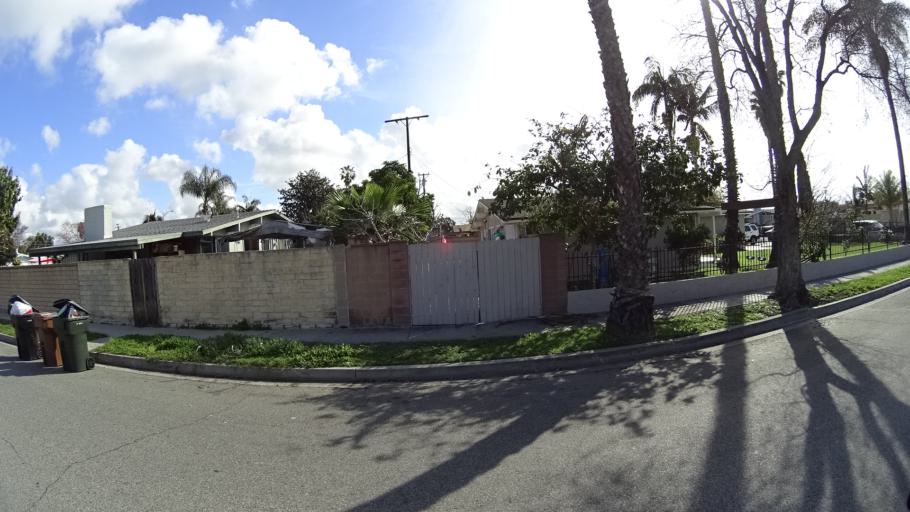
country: US
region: California
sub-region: Orange County
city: Stanton
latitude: 33.8301
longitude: -117.9713
